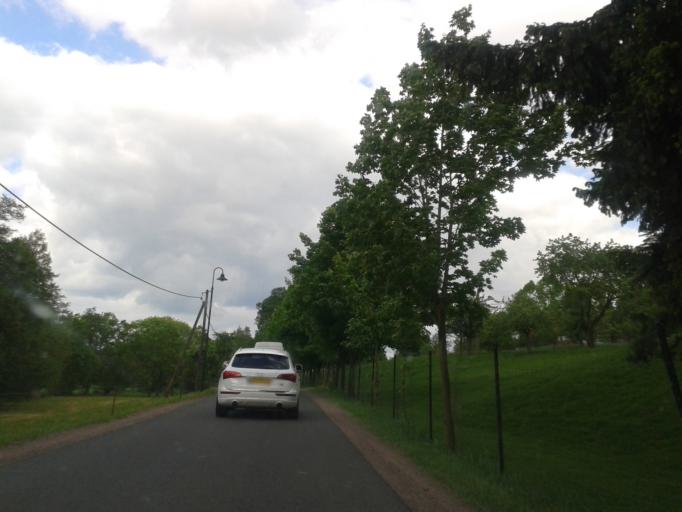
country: DE
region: Saxony
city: Klipphausen
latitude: 51.0786
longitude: 13.4883
